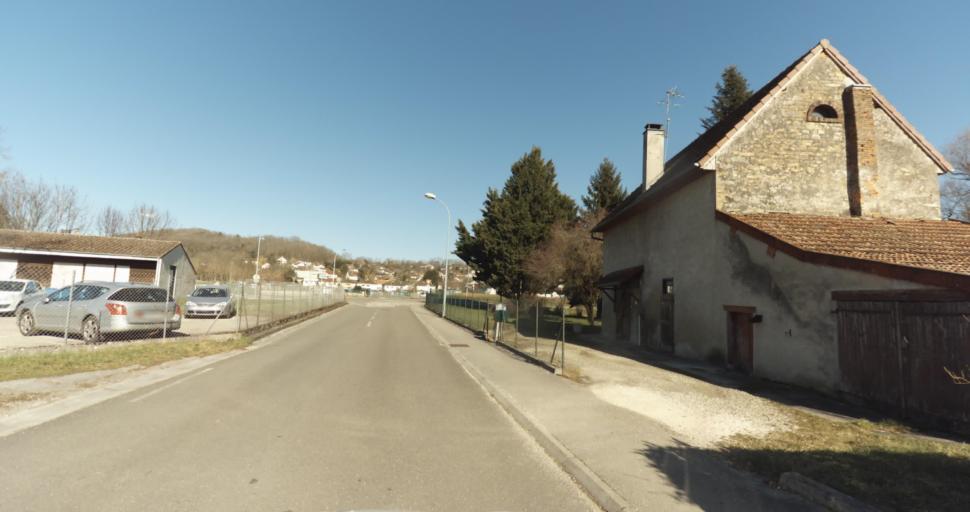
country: FR
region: Franche-Comte
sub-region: Departement du Jura
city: Montmorot
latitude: 46.6765
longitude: 5.5372
